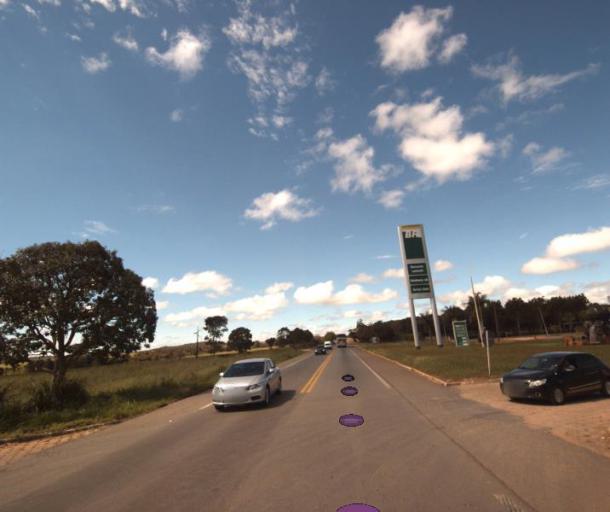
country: BR
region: Goias
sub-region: Rialma
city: Rialma
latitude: -15.4680
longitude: -49.4983
